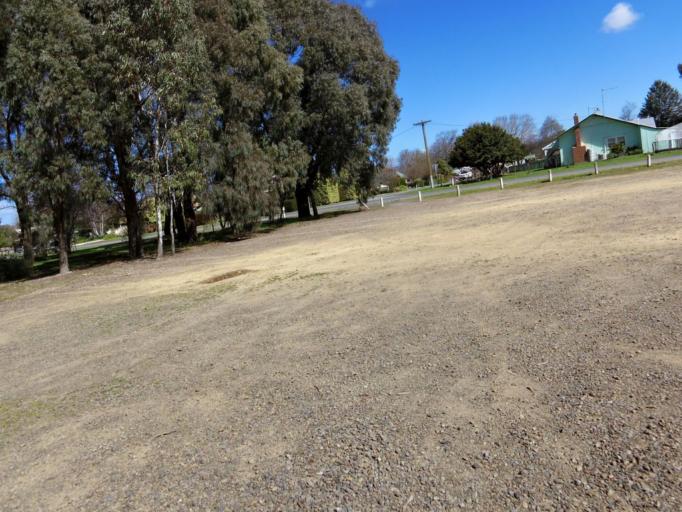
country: AU
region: Victoria
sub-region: Murrindindi
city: Alexandra
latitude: -37.1844
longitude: 145.7138
